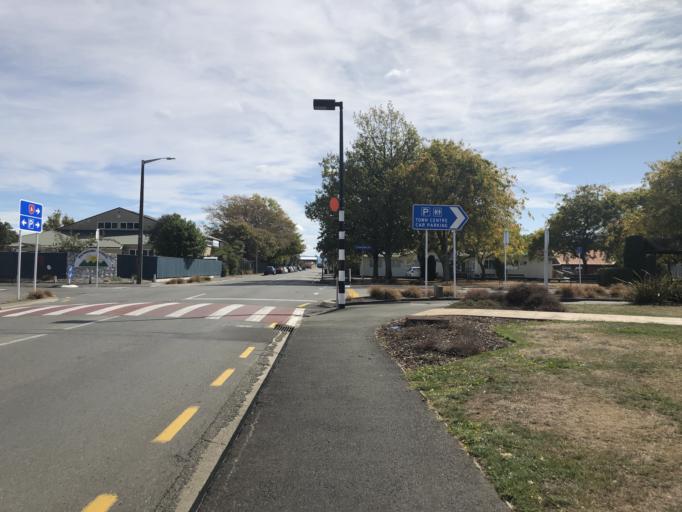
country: NZ
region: Tasman
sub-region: Tasman District
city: Richmond
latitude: -41.3395
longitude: 173.1828
